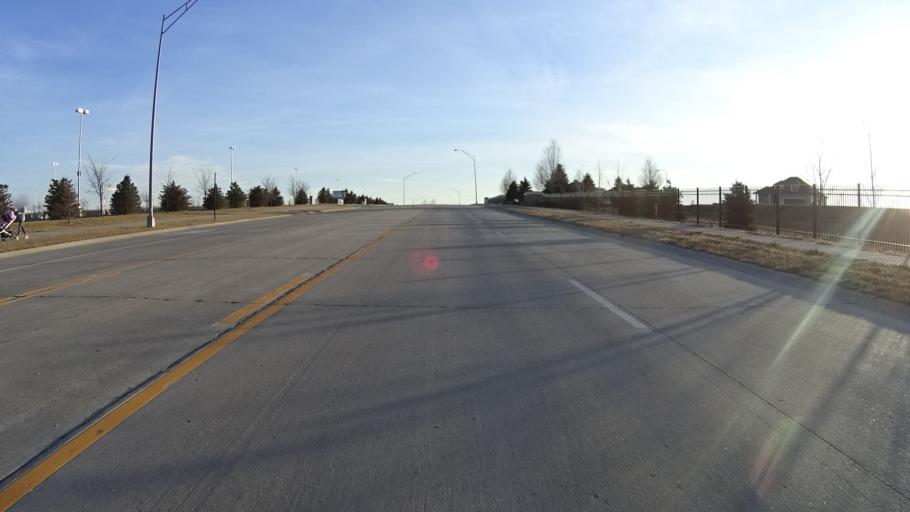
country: US
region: Nebraska
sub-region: Sarpy County
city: Chalco
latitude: 41.1531
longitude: -96.1099
